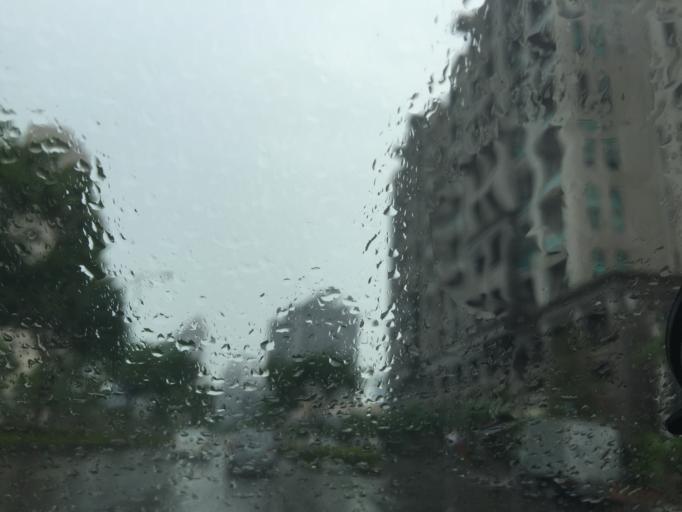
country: TW
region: Taiwan
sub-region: Hsinchu
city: Zhubei
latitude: 24.8142
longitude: 121.0331
